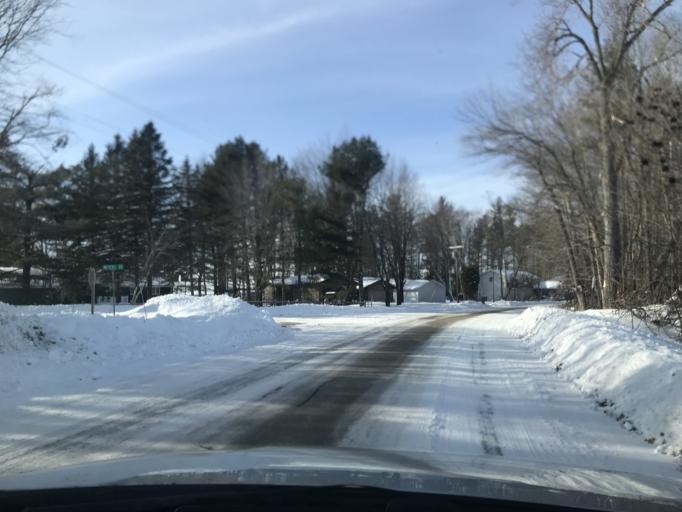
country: US
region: Wisconsin
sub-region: Oconto County
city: Oconto Falls
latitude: 45.1552
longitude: -88.1921
